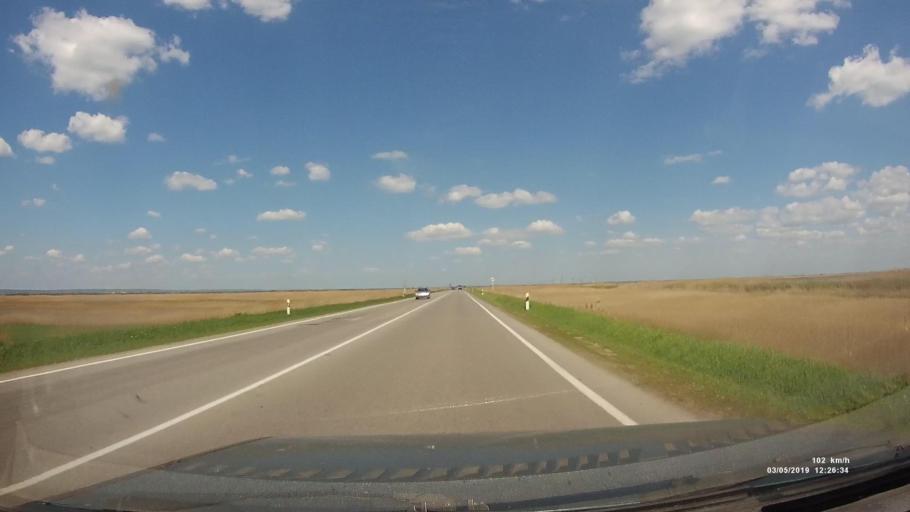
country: RU
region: Rostov
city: Semikarakorsk
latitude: 47.4472
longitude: 40.7147
